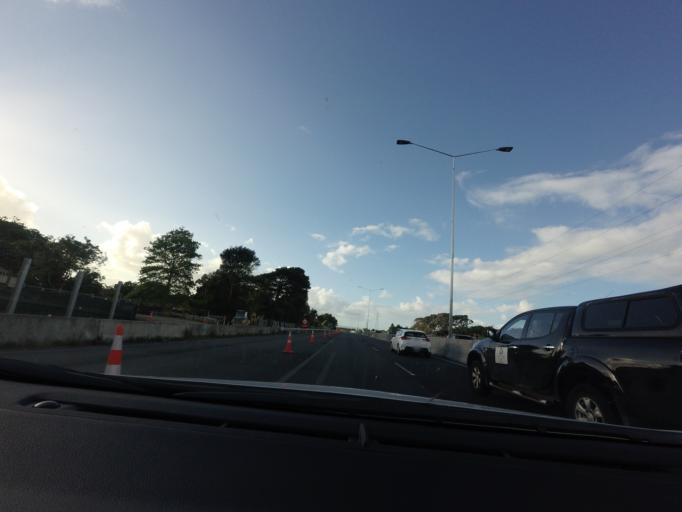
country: NZ
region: Auckland
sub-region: Auckland
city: Takanini
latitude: -37.0475
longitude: 174.9149
